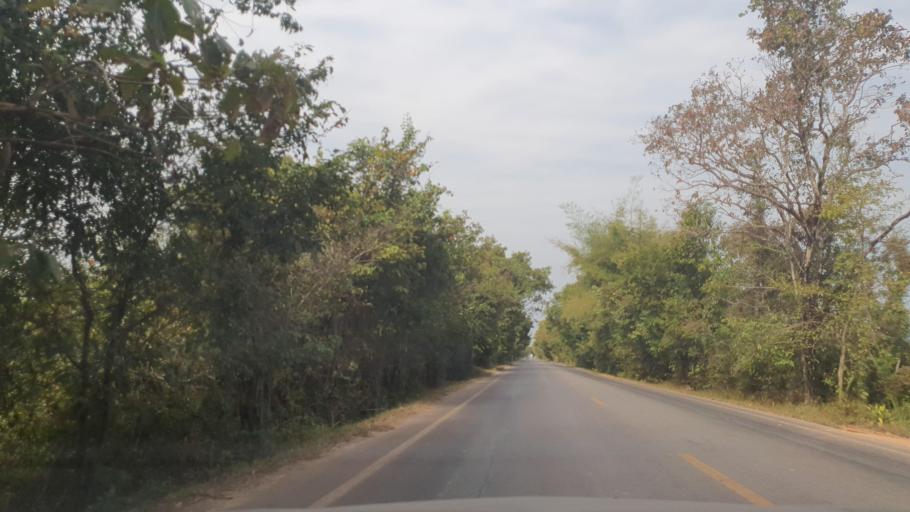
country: TH
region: Changwat Bueng Kan
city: Bung Khla
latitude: 18.2082
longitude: 104.0472
